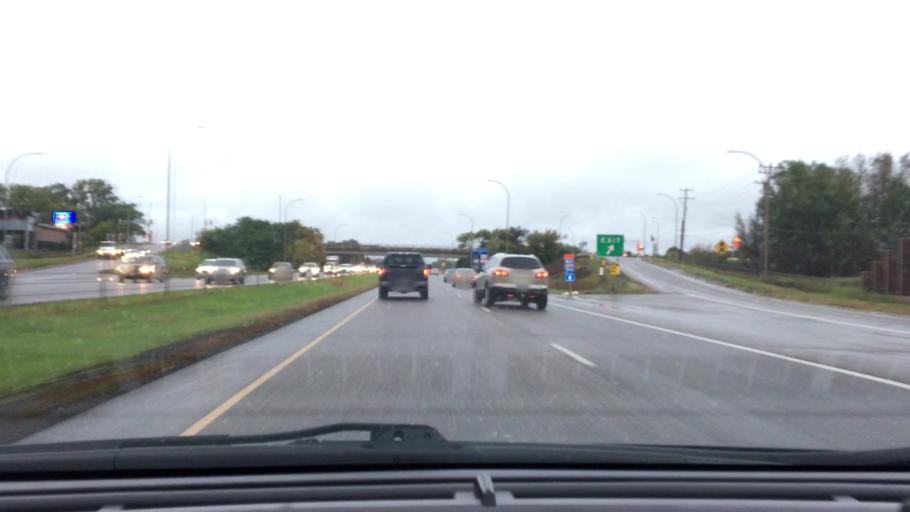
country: US
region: Minnesota
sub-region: Hennepin County
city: New Hope
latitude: 45.0417
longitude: -93.4008
